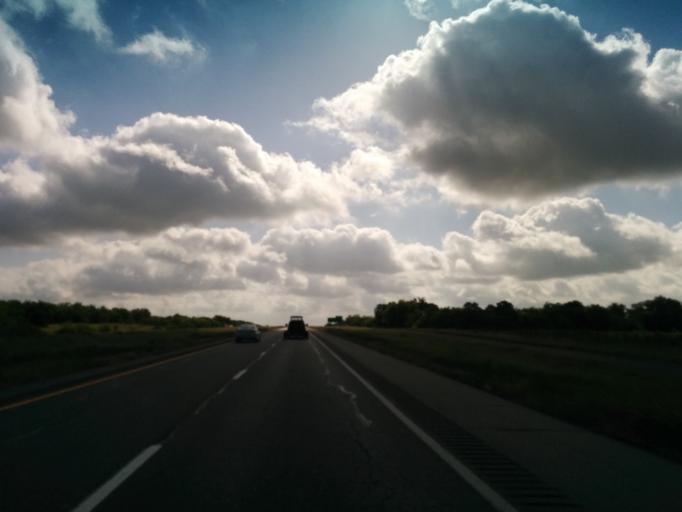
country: US
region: Texas
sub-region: Caldwell County
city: Luling
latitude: 29.6388
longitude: -97.7199
